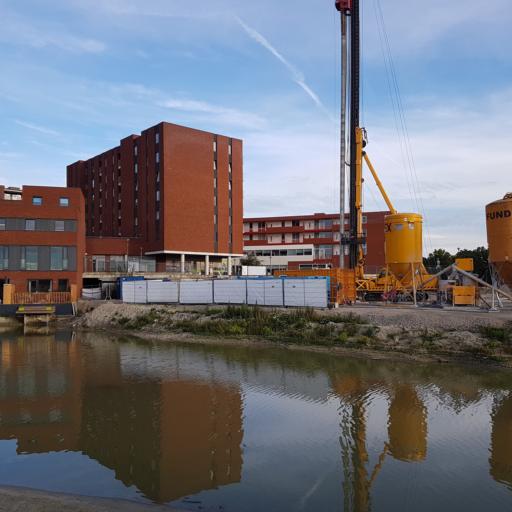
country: NL
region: North Brabant
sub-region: Gemeente Eindhoven
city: Meerhoven
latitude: 51.4429
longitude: 5.4069
